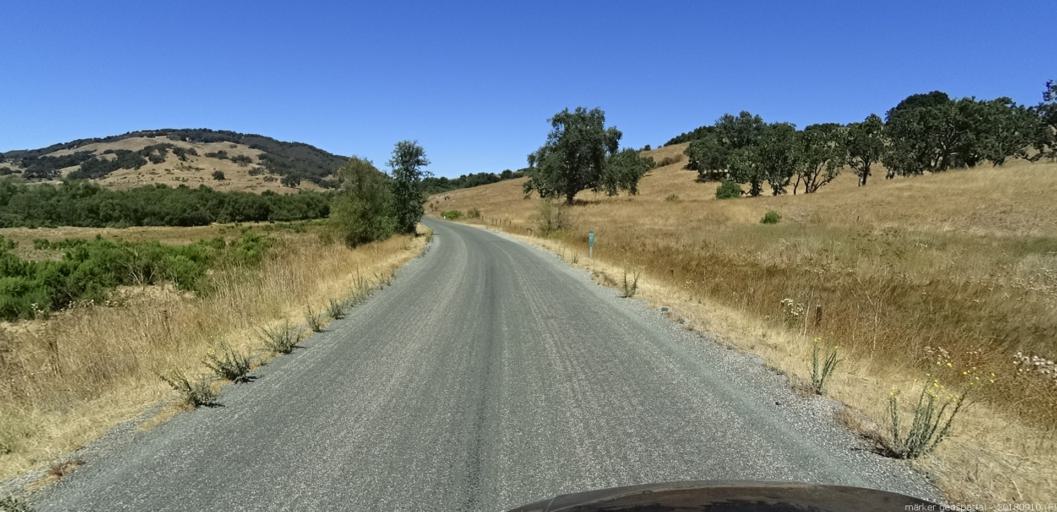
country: US
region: California
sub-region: Monterey County
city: Carmel Valley Village
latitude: 36.4553
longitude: -121.7968
